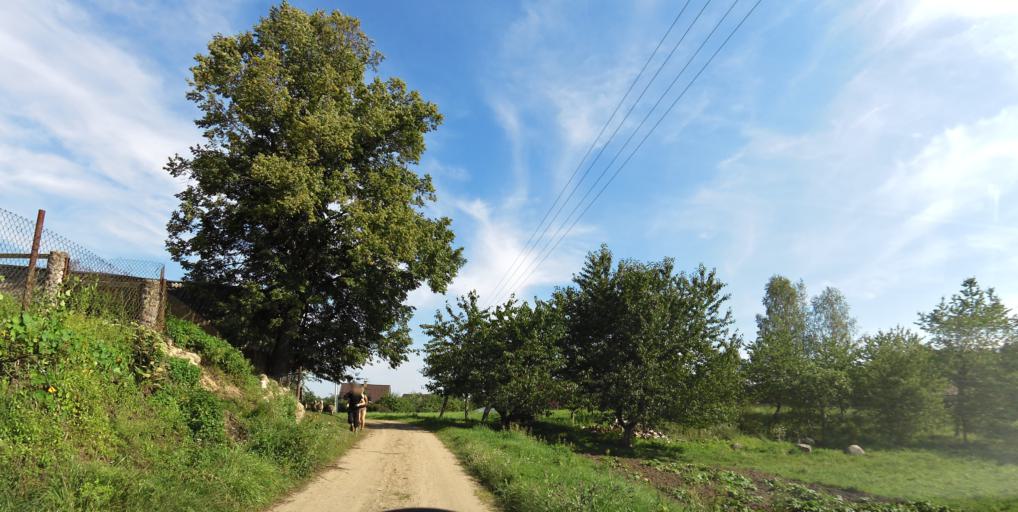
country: LT
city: Grigiskes
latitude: 54.7489
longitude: 25.0233
